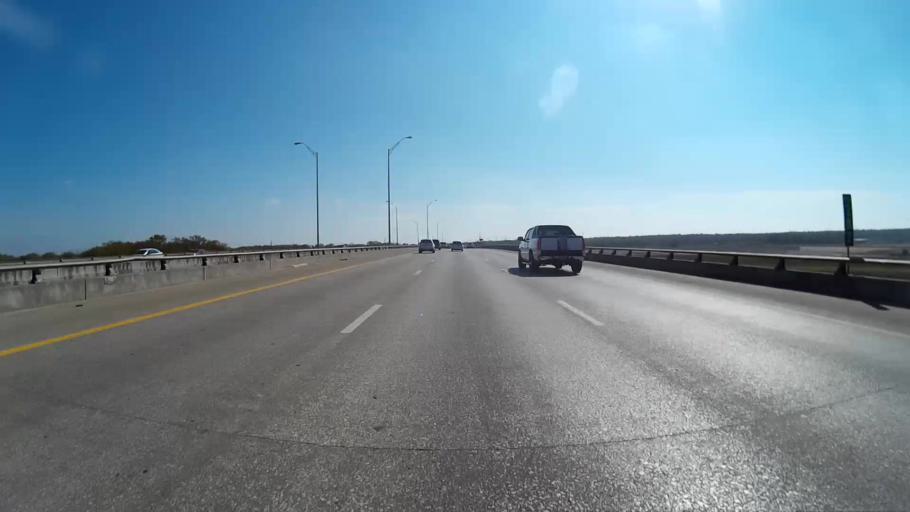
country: US
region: Texas
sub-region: Dallas County
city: Dallas
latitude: 32.7373
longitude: -96.7663
